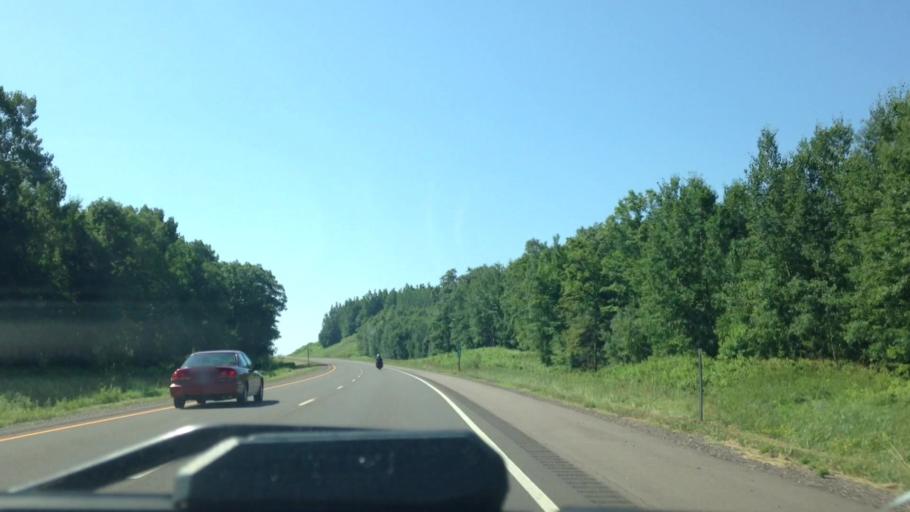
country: US
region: Wisconsin
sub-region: Washburn County
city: Spooner
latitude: 46.0117
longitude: -91.8370
